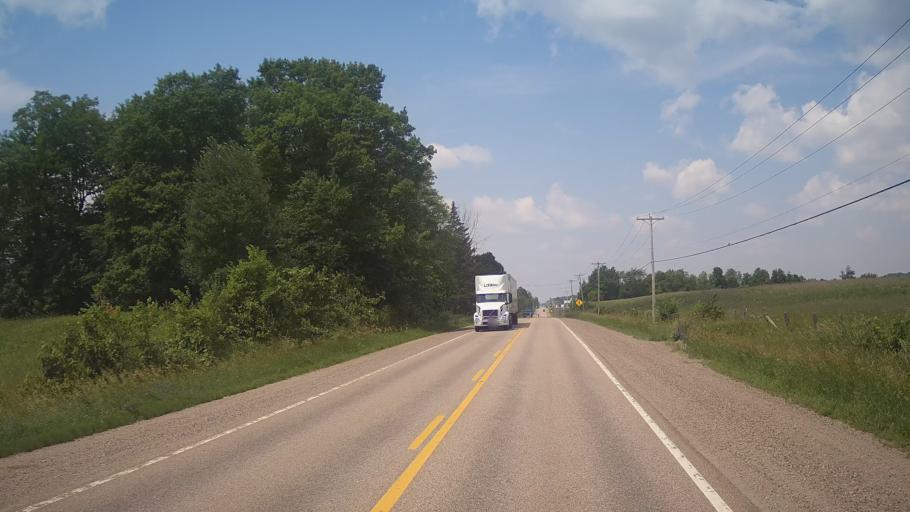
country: CA
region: Quebec
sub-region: Outaouais
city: Shawville
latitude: 45.5930
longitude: -76.4759
